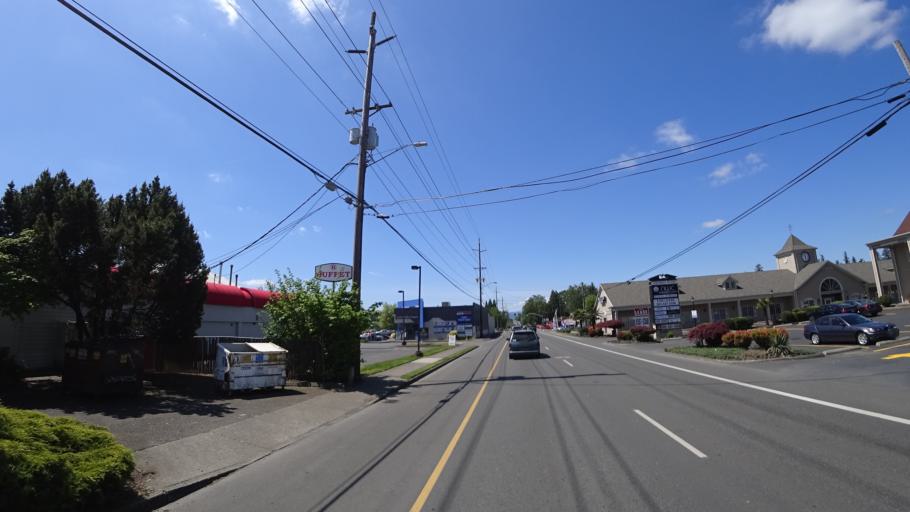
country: US
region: Oregon
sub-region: Washington County
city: Hillsboro
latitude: 45.5199
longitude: -123.0008
